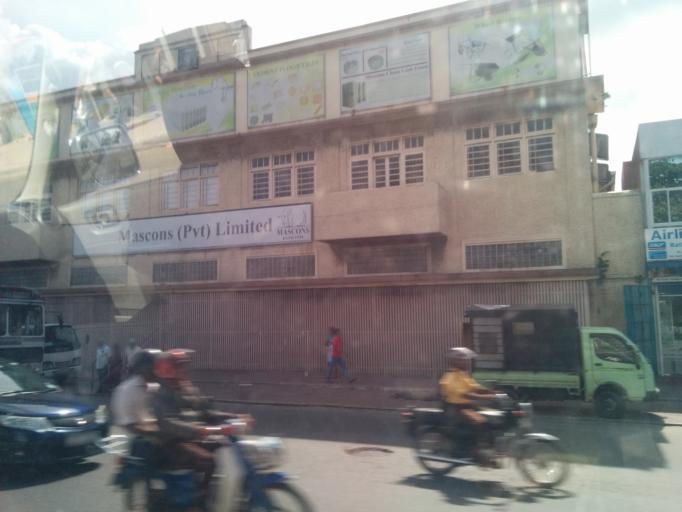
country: LK
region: Western
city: Colombo
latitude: 6.9403
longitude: 79.8656
